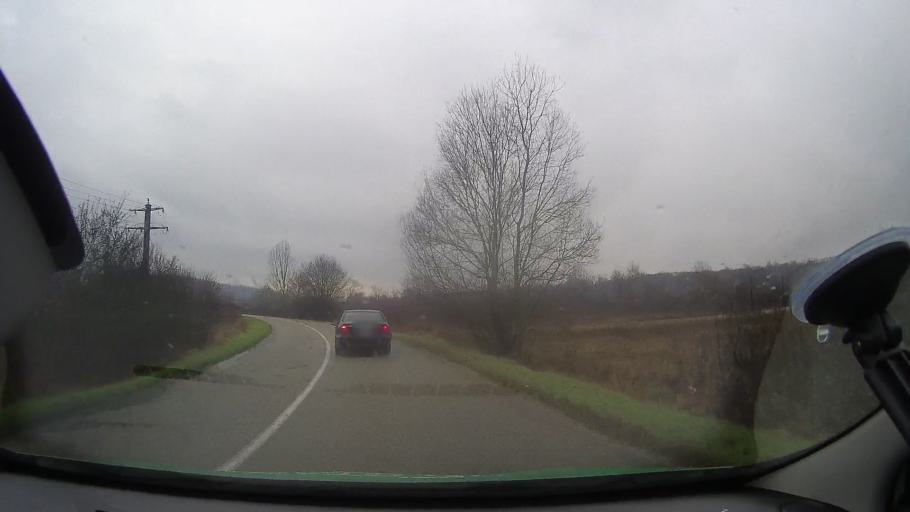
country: RO
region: Arad
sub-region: Comuna Ignesti
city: Ignesti
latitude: 46.3867
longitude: 22.1658
